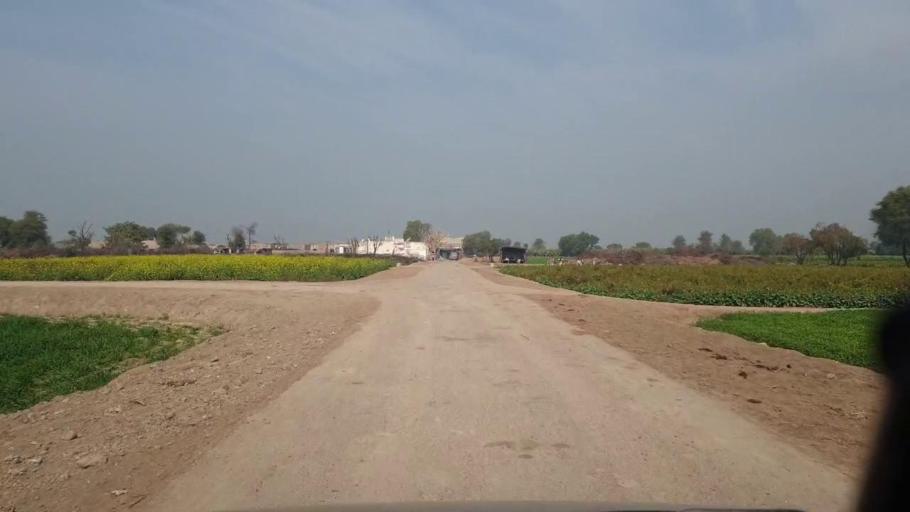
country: PK
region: Sindh
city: Shahdadpur
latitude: 26.0119
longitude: 68.5102
